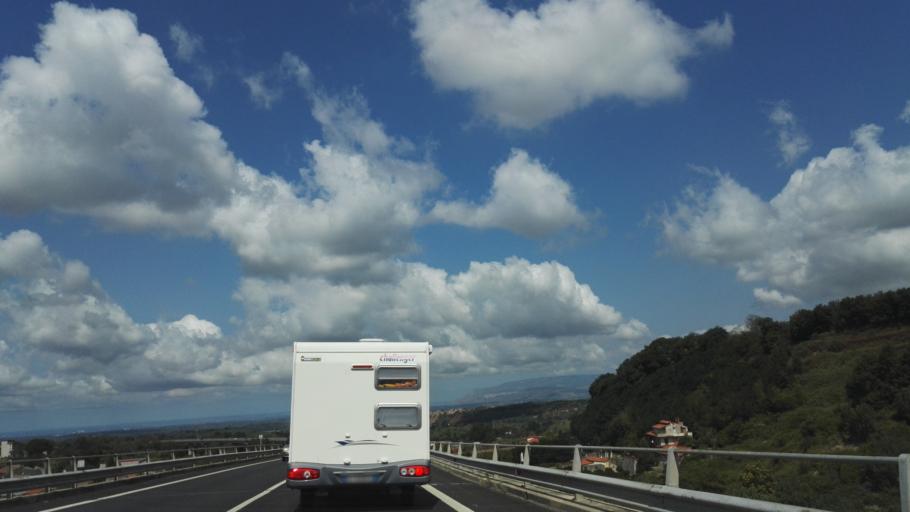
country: IT
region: Calabria
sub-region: Provincia di Reggio Calabria
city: Anoia Superiore
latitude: 38.4181
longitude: 16.1036
